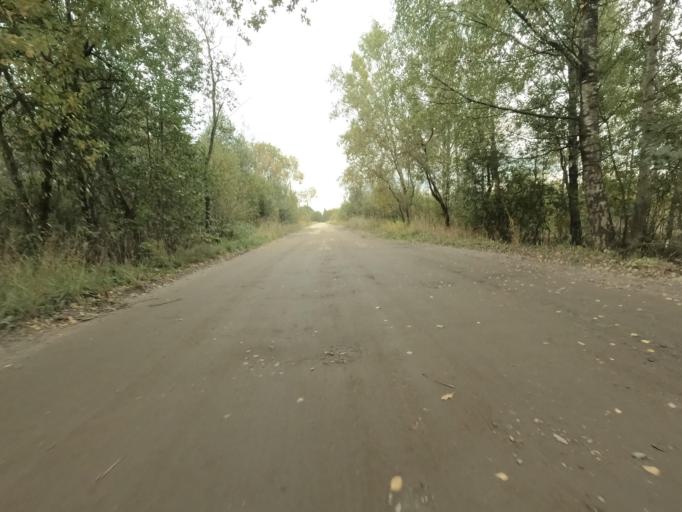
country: RU
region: St.-Petersburg
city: Sapernyy
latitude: 59.7601
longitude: 30.6550
